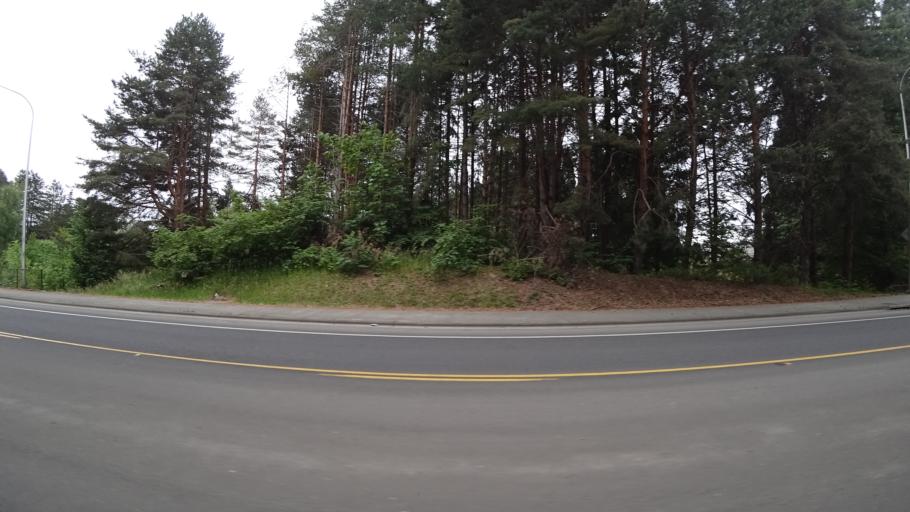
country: US
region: Oregon
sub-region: Washington County
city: Hillsboro
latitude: 45.4951
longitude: -122.9405
